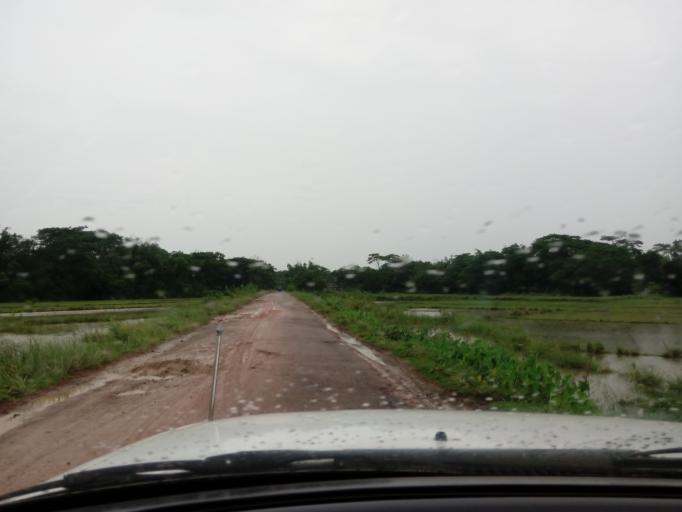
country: BD
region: Sylhet
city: Sylhet
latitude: 24.9636
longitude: 91.7945
